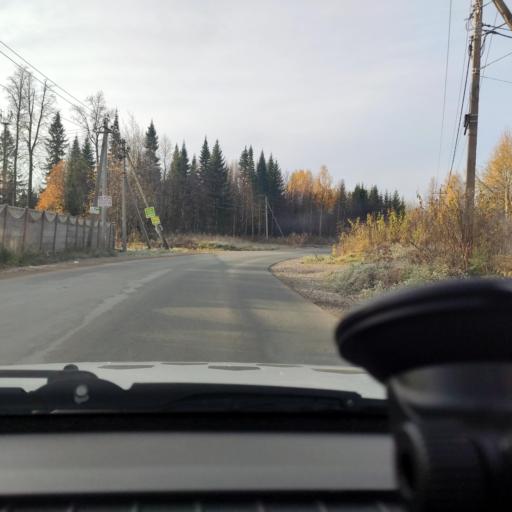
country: RU
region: Perm
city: Ferma
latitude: 57.9405
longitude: 56.4209
